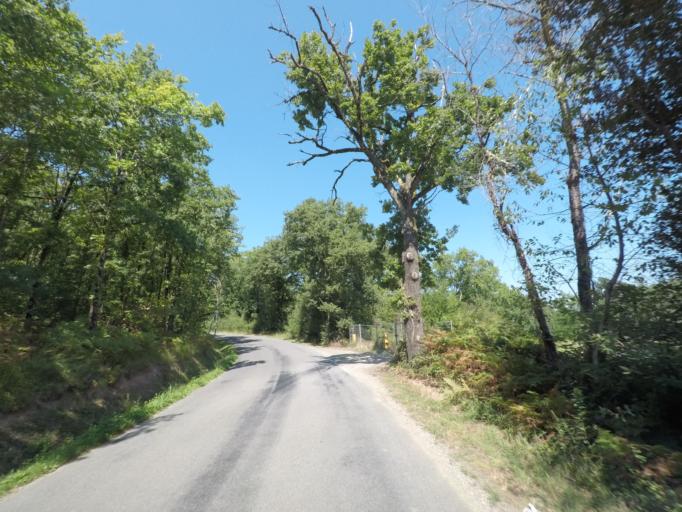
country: FR
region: Midi-Pyrenees
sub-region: Departement de l'Aveyron
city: Livinhac-le-Haut
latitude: 44.6081
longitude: 2.2284
